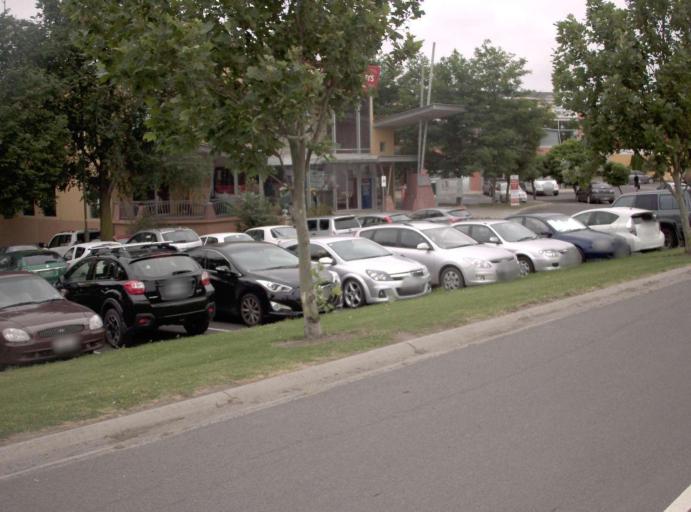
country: AU
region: Victoria
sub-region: Latrobe
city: Traralgon
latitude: -38.1970
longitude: 146.5410
